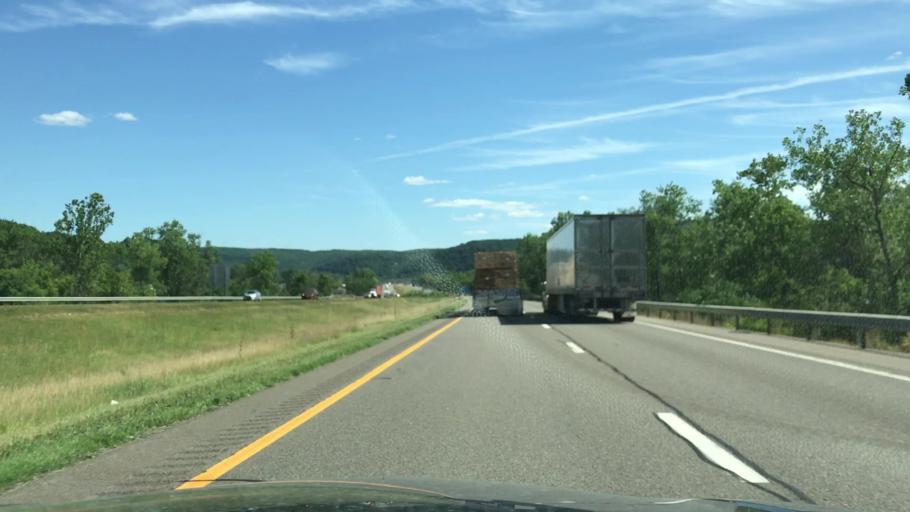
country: US
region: New York
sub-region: Steuben County
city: Bath
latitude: 42.3548
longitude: -77.3473
